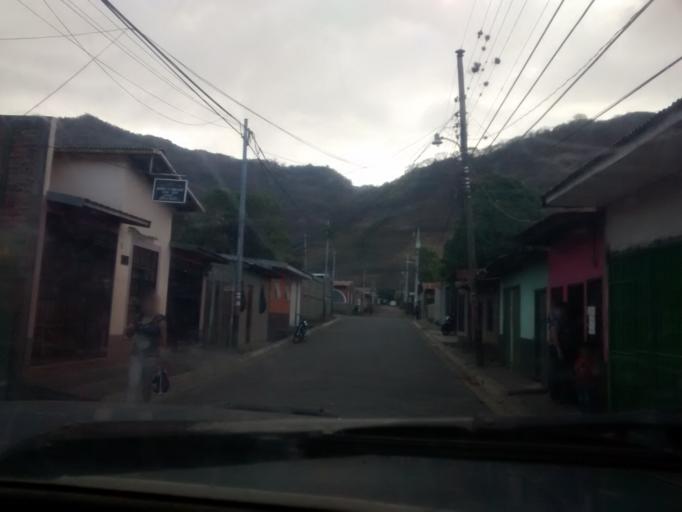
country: NI
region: Jinotega
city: Jinotega
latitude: 13.0870
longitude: -86.0040
